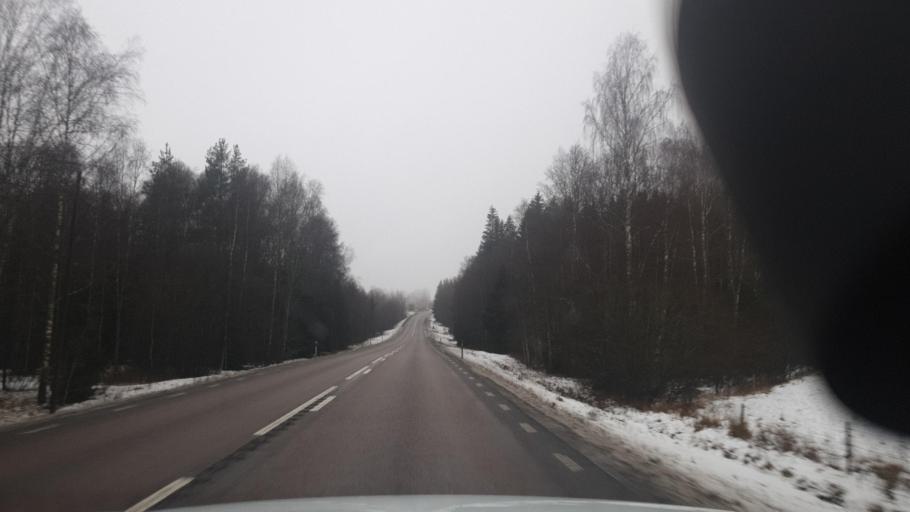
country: SE
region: Vaermland
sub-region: Sunne Kommun
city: Sunne
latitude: 59.6671
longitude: 12.9014
